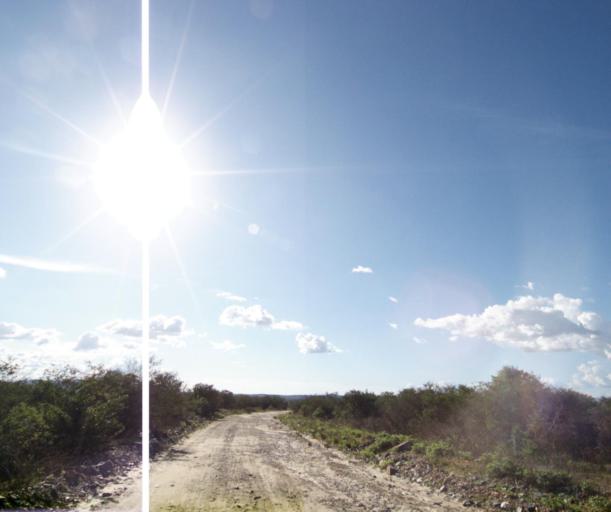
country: BR
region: Bahia
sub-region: Tanhacu
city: Tanhacu
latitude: -14.1874
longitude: -40.9851
